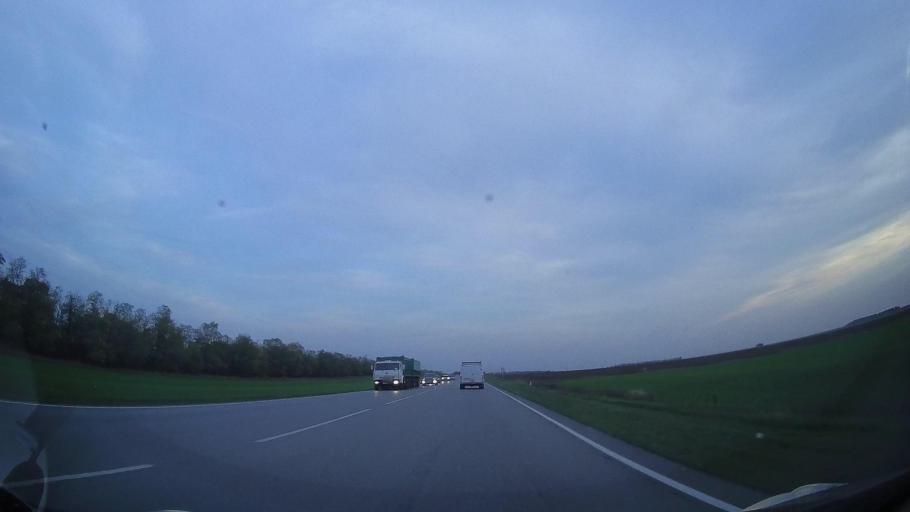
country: RU
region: Rostov
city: Kagal'nitskaya
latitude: 46.9045
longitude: 40.1195
